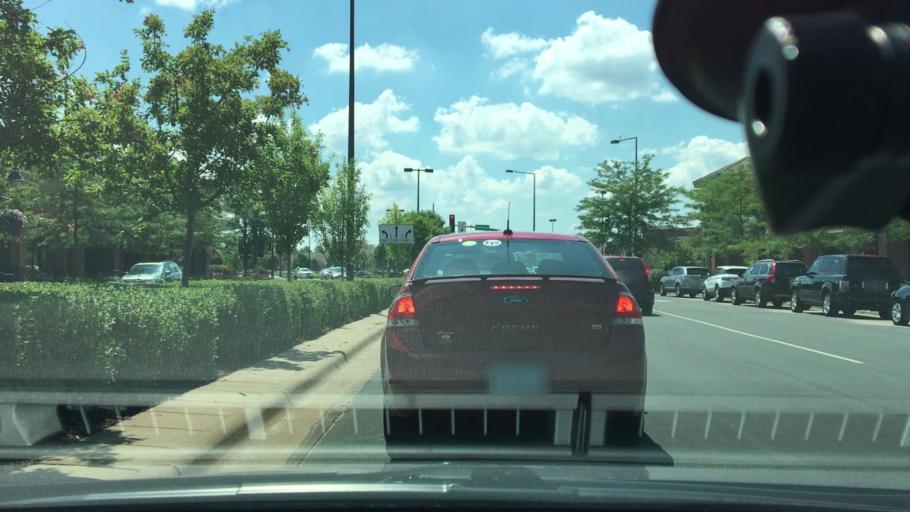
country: US
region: Minnesota
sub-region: Hennepin County
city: Maple Grove
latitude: 45.0934
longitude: -93.4270
